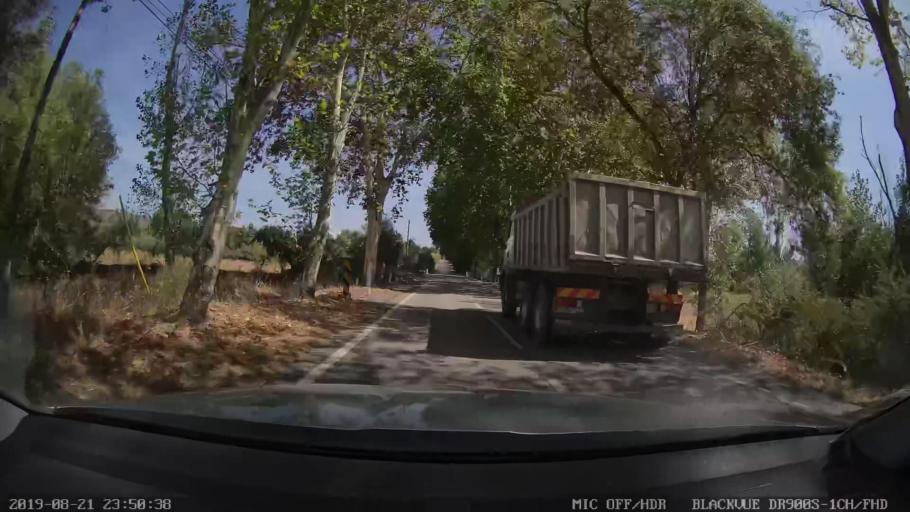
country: PT
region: Castelo Branco
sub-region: Idanha-A-Nova
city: Idanha-a-Nova
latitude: 39.8925
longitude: -7.2409
